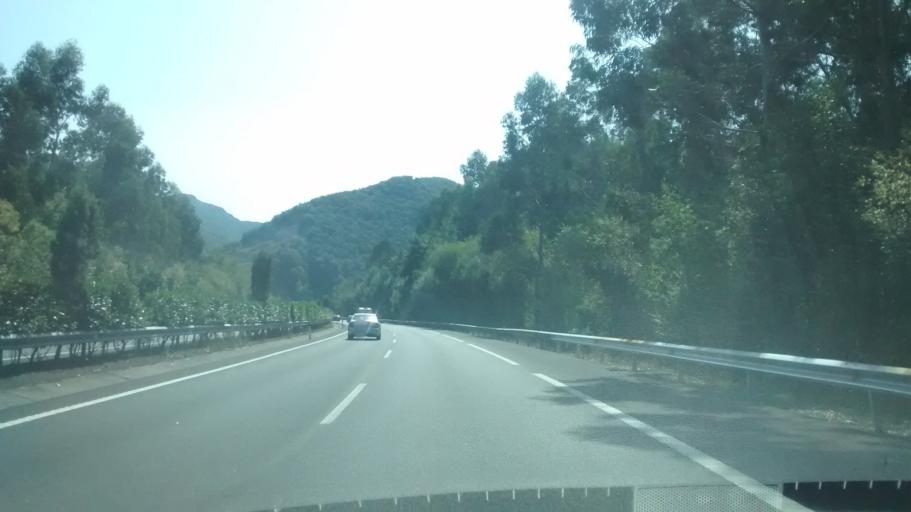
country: ES
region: Cantabria
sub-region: Provincia de Cantabria
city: Liendo
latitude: 43.3827
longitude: -3.3820
